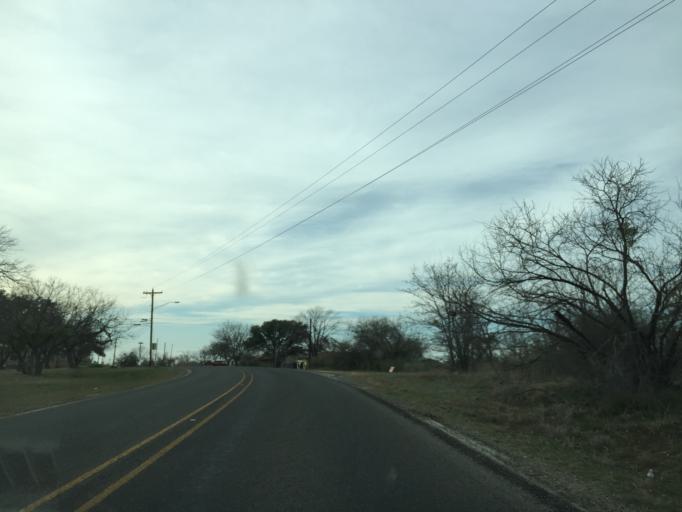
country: US
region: Texas
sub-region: Llano County
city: Llano
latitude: 30.7511
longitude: -98.6853
